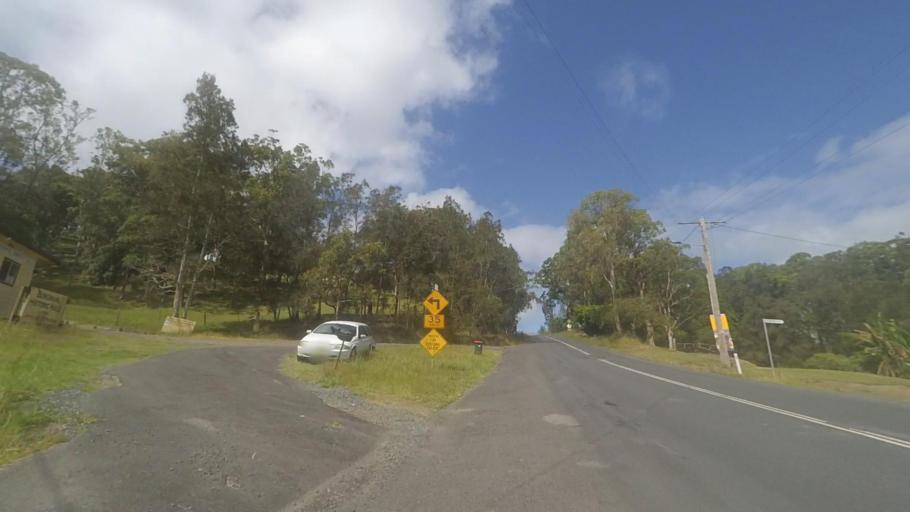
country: AU
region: New South Wales
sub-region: Great Lakes
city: Forster
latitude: -32.3935
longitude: 152.4389
